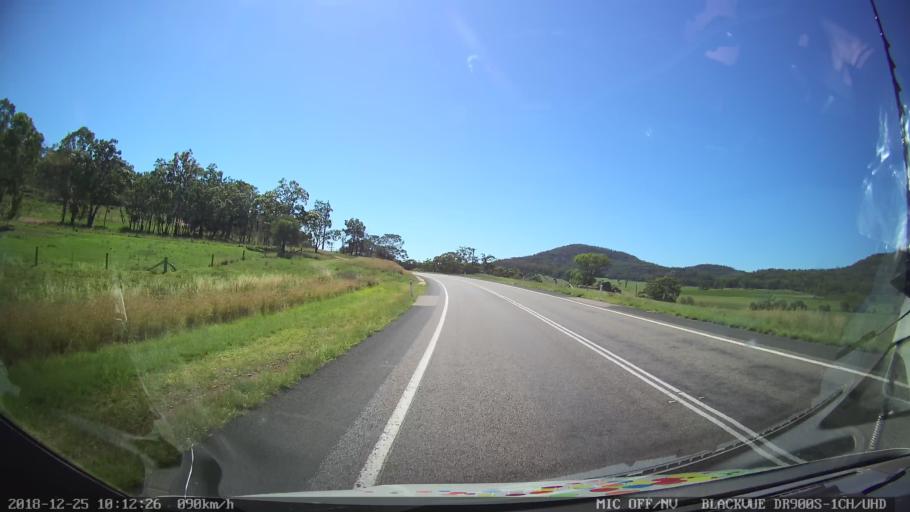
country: AU
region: New South Wales
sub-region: Muswellbrook
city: Denman
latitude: -32.3283
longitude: 150.5315
